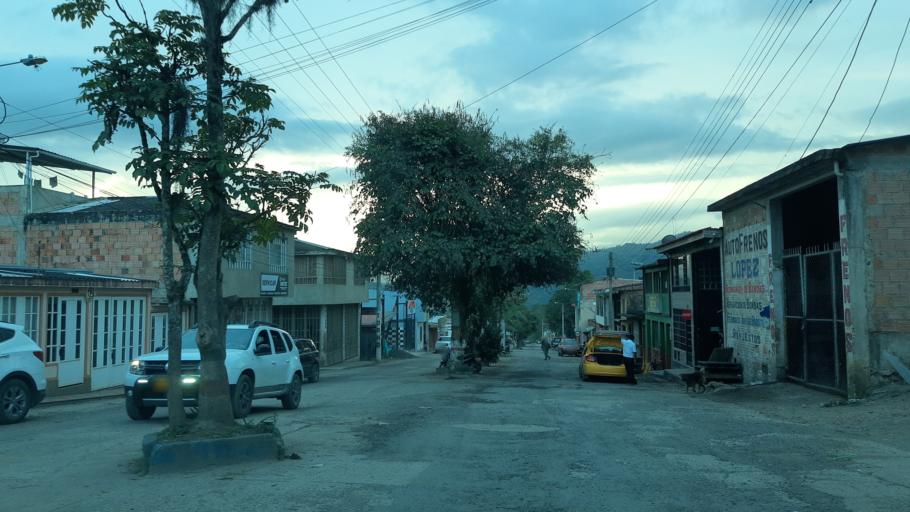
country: CO
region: Boyaca
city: Garagoa
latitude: 5.0859
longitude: -73.3641
